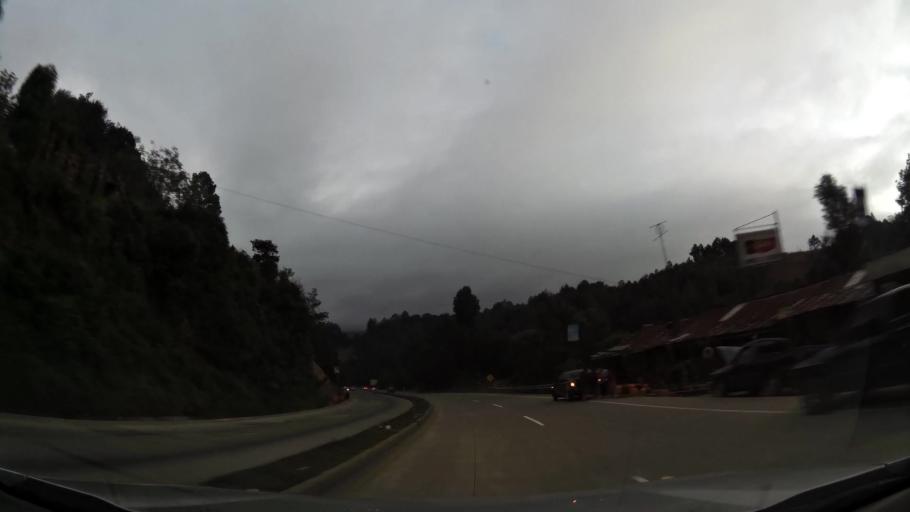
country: GT
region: Quiche
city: Chichicastenango
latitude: 14.8573
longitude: -91.0566
